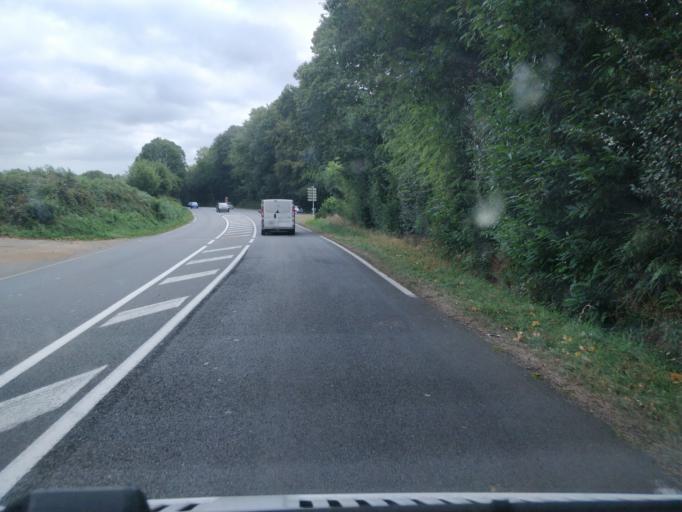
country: FR
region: Brittany
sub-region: Departement du Finistere
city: Pluguffan
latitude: 47.9991
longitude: -4.1650
